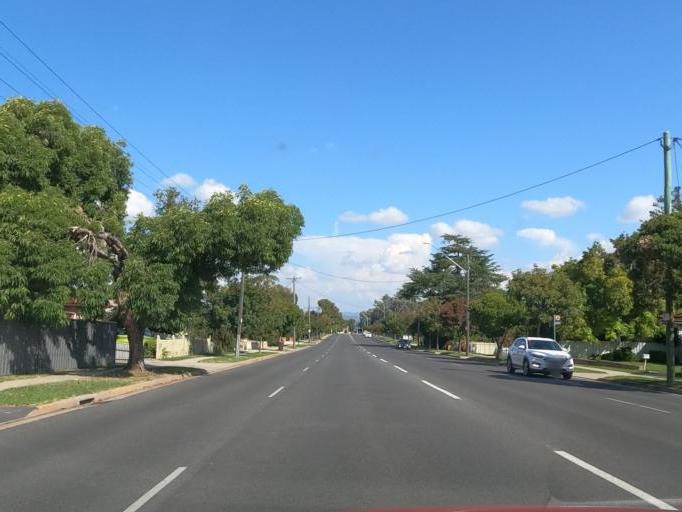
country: AU
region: New South Wales
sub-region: Albury Municipality
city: North Albury
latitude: -36.0584
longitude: 146.9270
